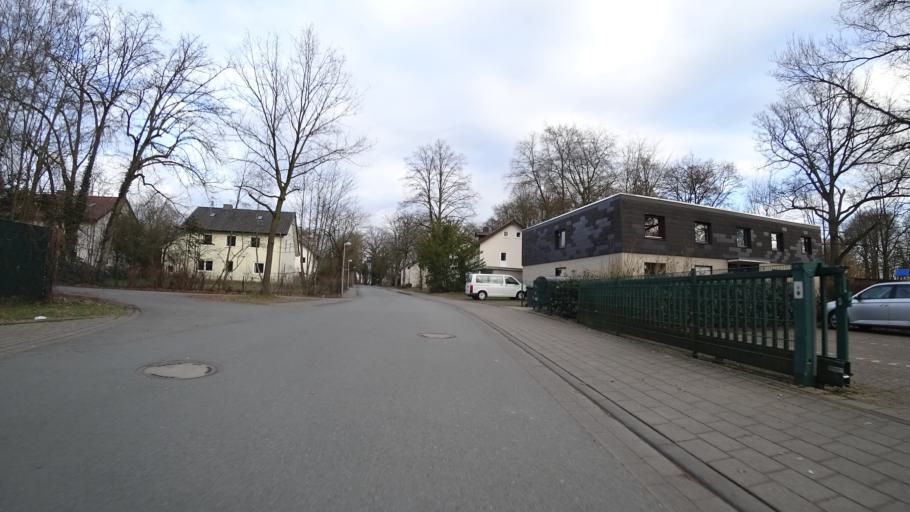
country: DE
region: North Rhine-Westphalia
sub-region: Regierungsbezirk Detmold
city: Guetersloh
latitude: 51.9001
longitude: 8.3953
